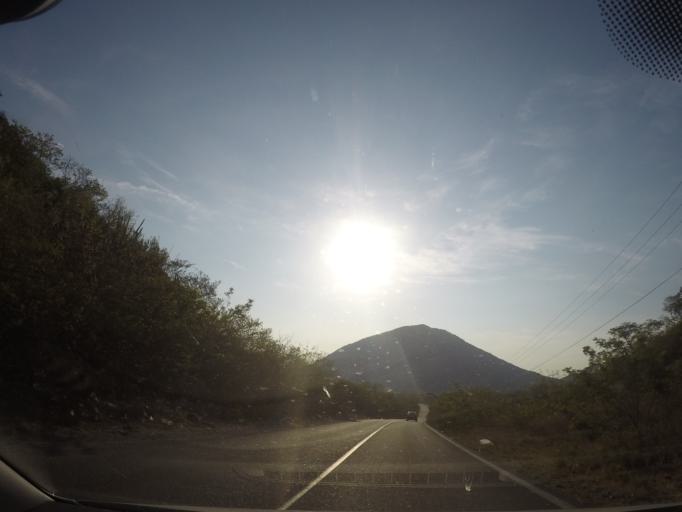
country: MX
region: Oaxaca
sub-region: Santo Domingo Tehuantepec
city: La Noria
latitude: 16.2364
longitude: -95.1644
